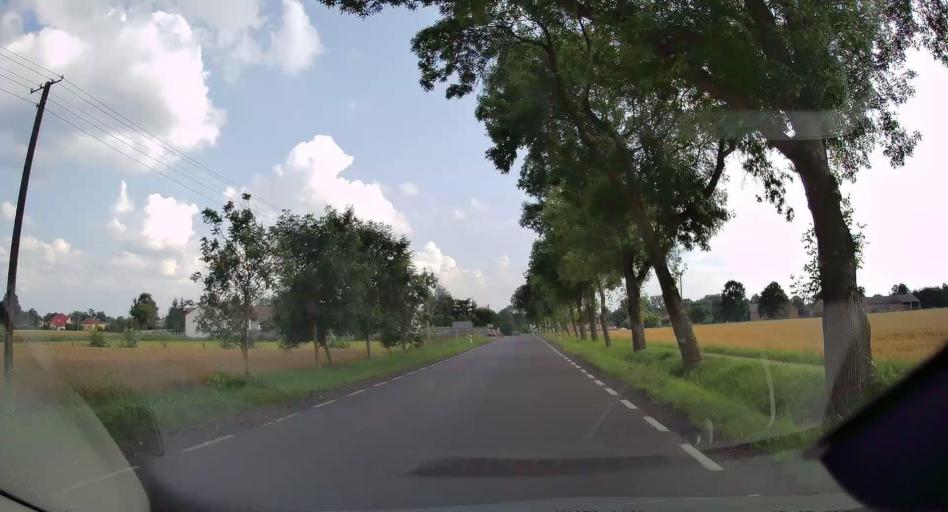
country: PL
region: Lodz Voivodeship
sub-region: Powiat tomaszowski
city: Rzeczyca
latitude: 51.6027
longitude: 20.2937
